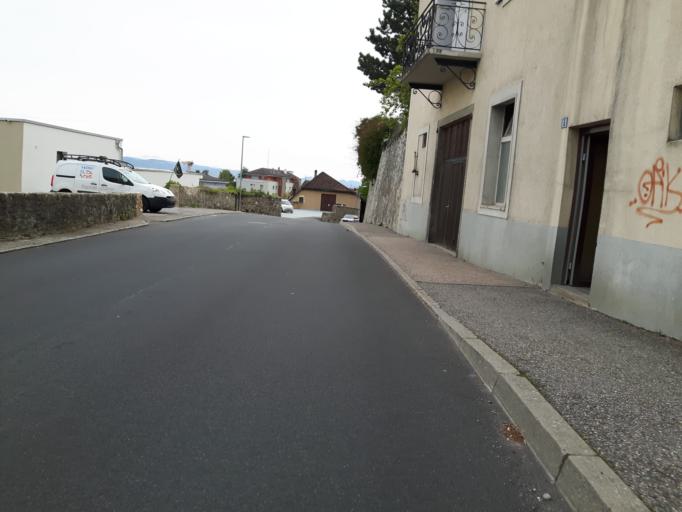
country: CH
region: Neuchatel
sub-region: Boudry District
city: Saint-Aubin-Sauges
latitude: 46.8972
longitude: 6.7757
